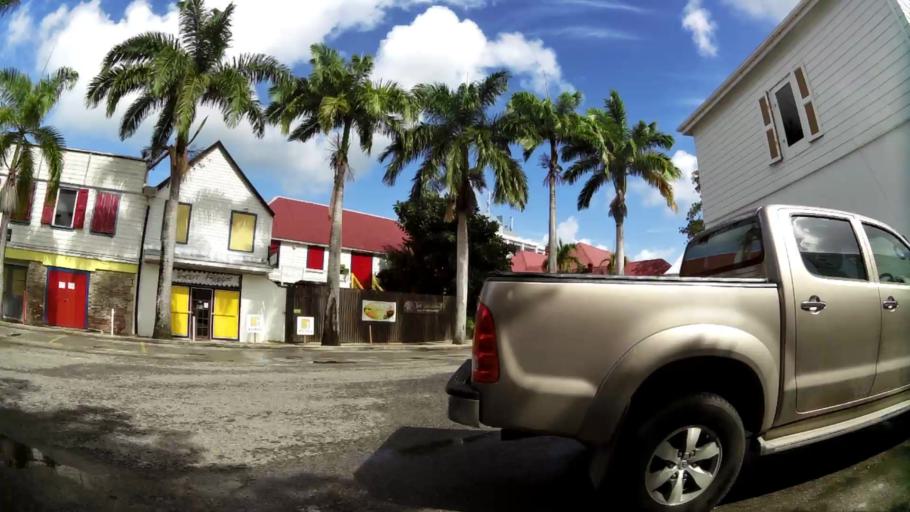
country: AG
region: Saint John
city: Saint John's
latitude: 17.1202
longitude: -61.8459
